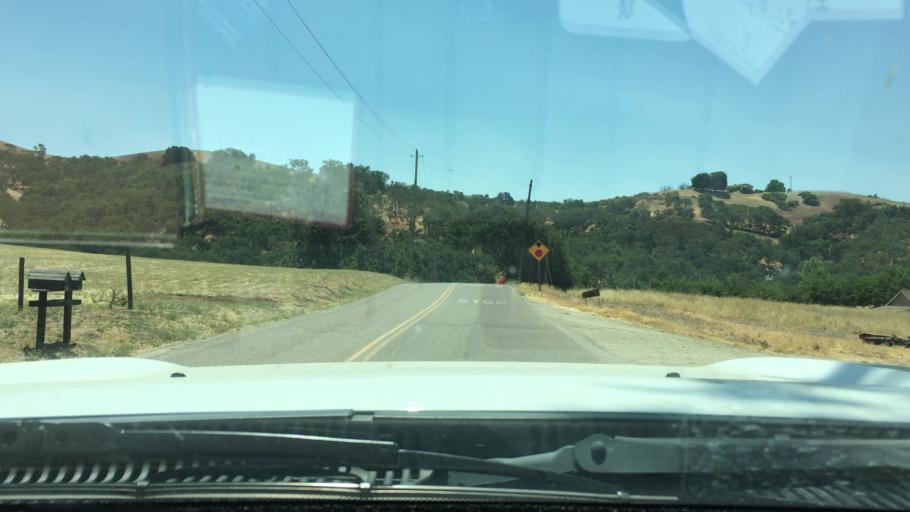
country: US
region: California
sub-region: San Luis Obispo County
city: Atascadero
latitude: 35.5124
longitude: -120.6390
